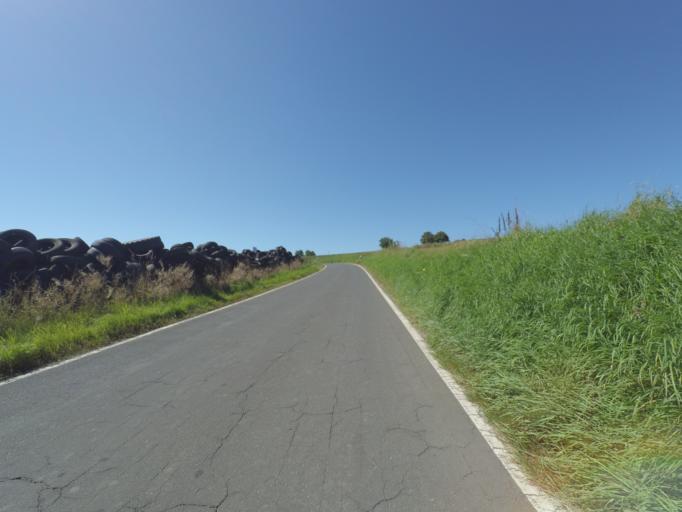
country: DE
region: Rheinland-Pfalz
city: Schladt
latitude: 50.0409
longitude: 6.8408
